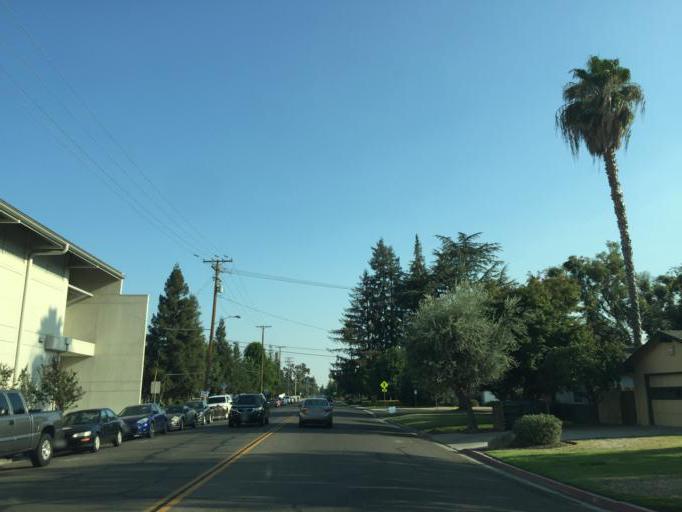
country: US
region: California
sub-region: Tulare County
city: Visalia
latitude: 36.3251
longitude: -119.3185
